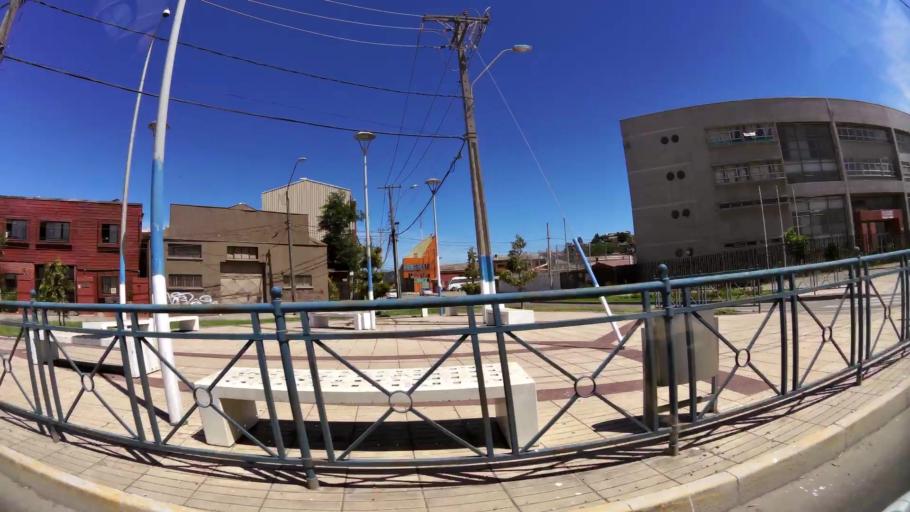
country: CL
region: Biobio
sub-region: Provincia de Concepcion
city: Talcahuano
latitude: -36.7219
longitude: -73.1088
